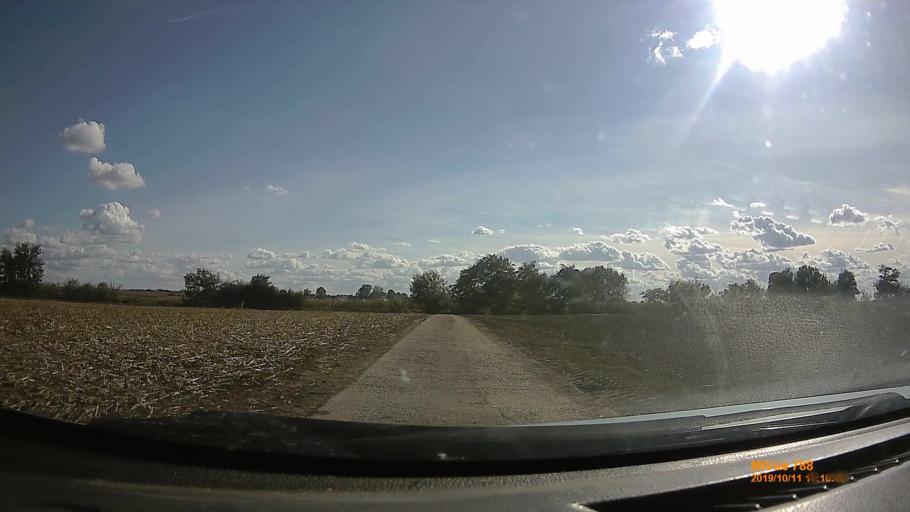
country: HU
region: Hajdu-Bihar
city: Hajduszoboszlo
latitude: 47.5306
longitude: 21.4017
